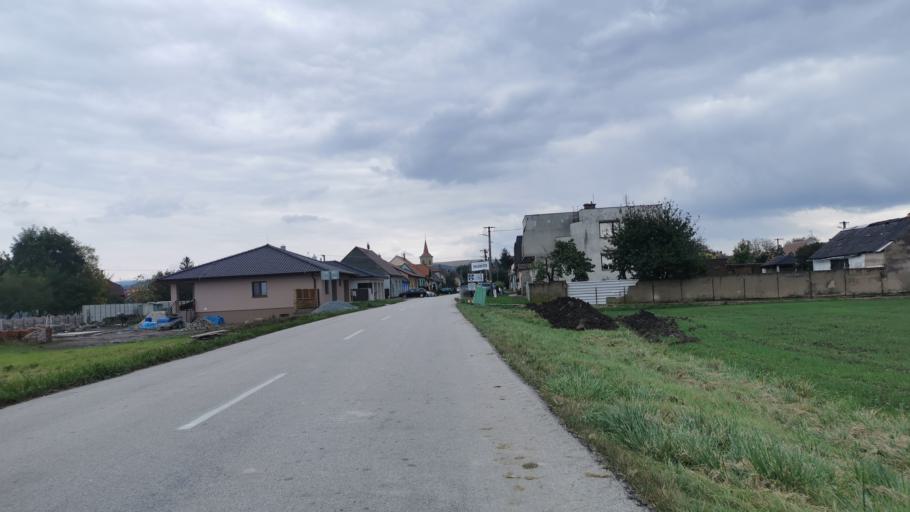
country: SK
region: Trnavsky
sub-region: Okres Skalica
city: Holic
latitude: 48.8260
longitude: 17.1875
